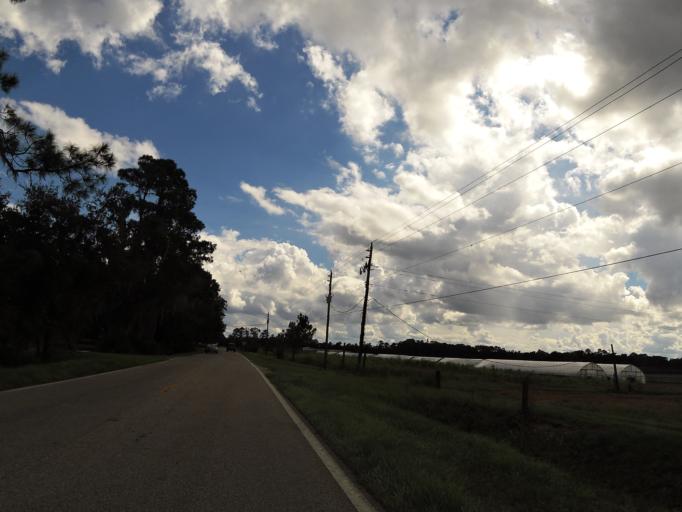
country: US
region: Florida
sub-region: Putnam County
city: East Palatka
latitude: 29.7550
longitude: -81.4758
